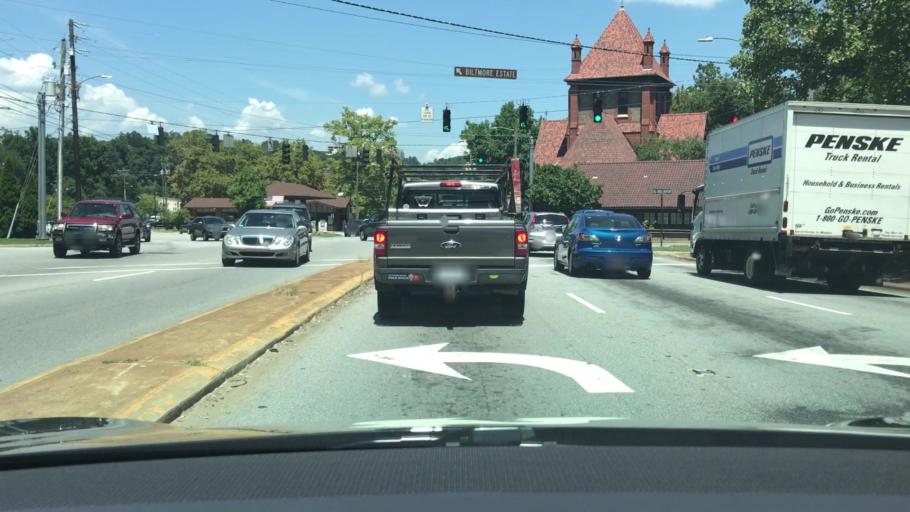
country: US
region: North Carolina
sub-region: Buncombe County
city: Biltmore Forest
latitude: 35.5646
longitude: -82.5427
